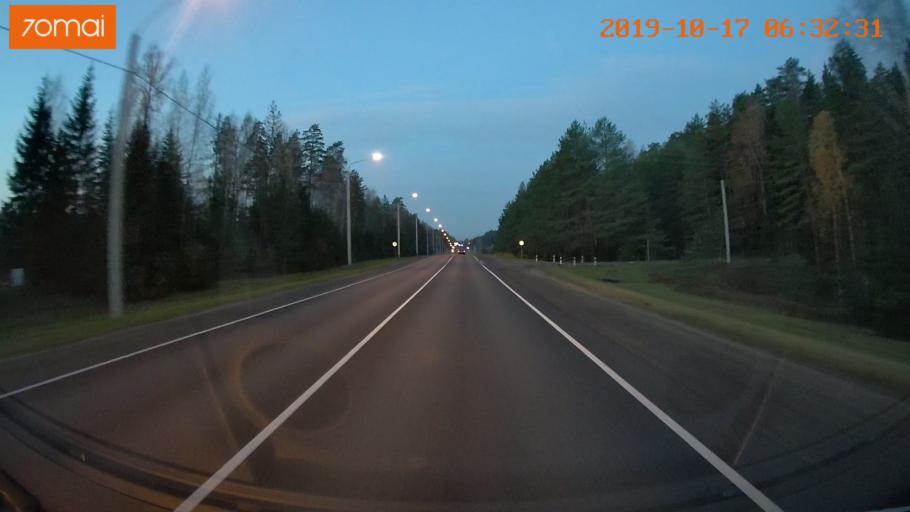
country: RU
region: Ivanovo
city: Novoye Leushino
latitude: 56.7191
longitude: 40.6752
